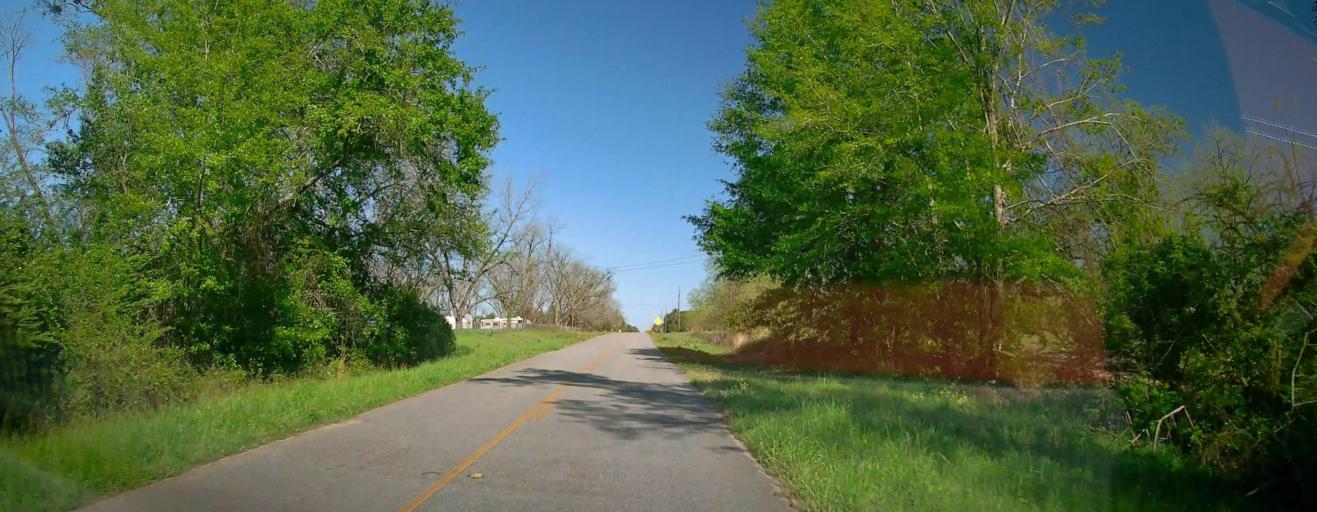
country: US
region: Georgia
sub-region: Pulaski County
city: Hawkinsville
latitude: 32.2477
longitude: -83.4767
